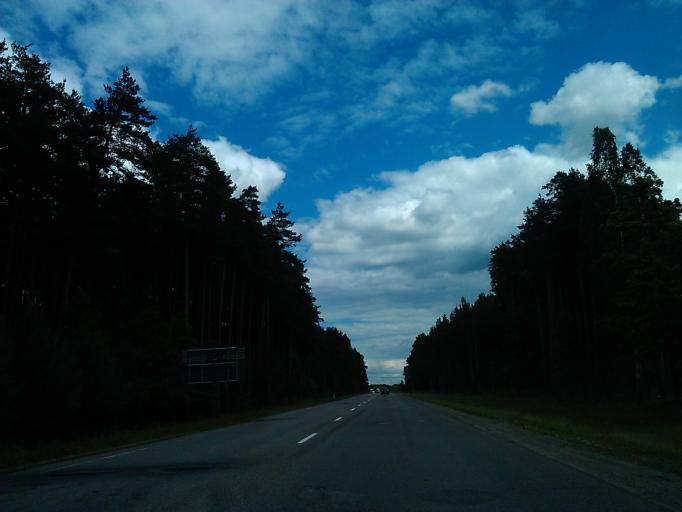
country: LV
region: Jelgava
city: Jelgava
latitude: 56.6314
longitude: 23.7580
